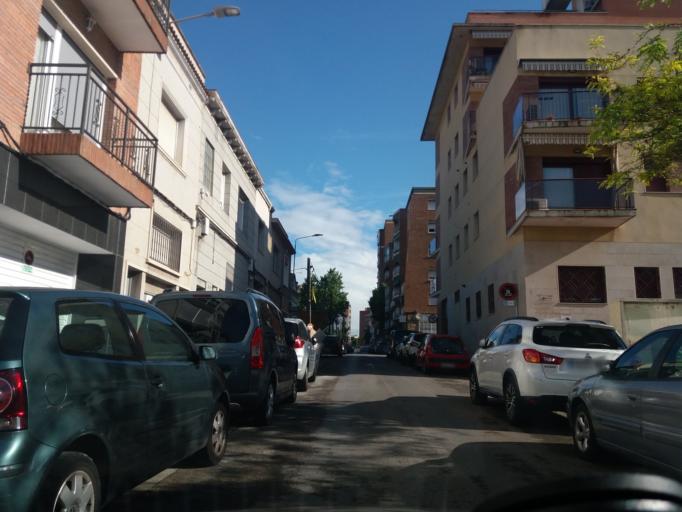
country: ES
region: Catalonia
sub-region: Provincia de Barcelona
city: Sabadell
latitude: 41.5583
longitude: 2.1006
